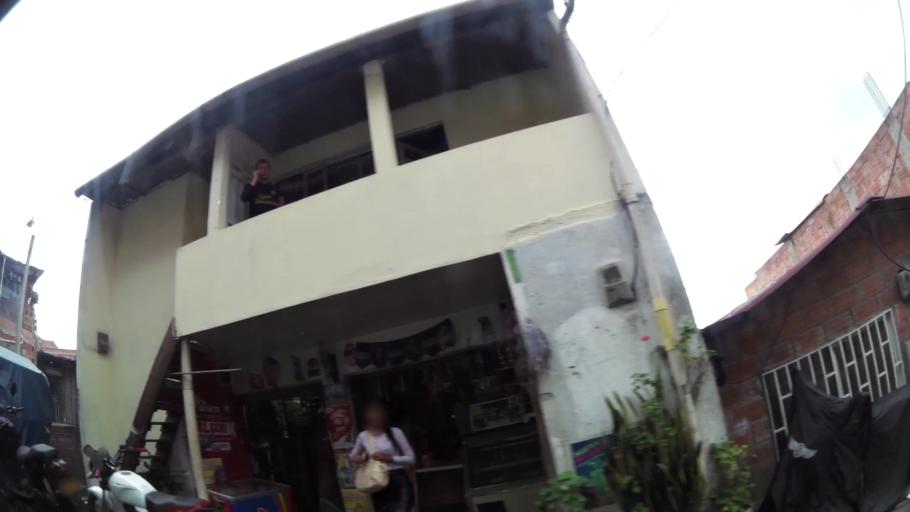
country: CO
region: Antioquia
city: Medellin
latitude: 6.2676
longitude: -75.6131
